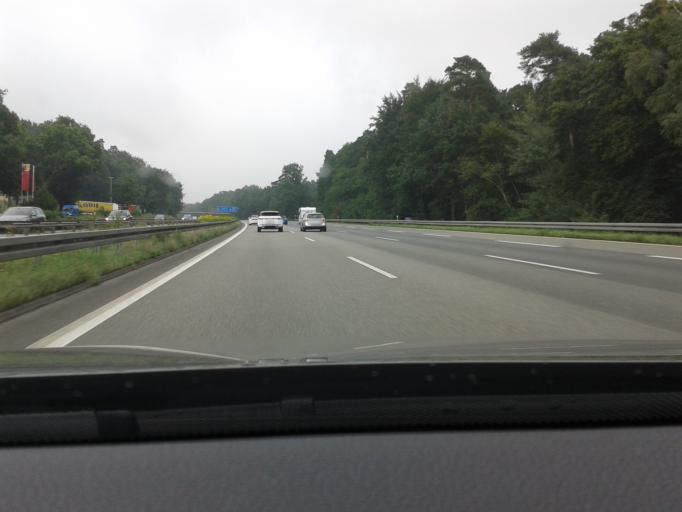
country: DE
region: North Rhine-Westphalia
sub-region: Regierungsbezirk Detmold
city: Verl
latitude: 51.9264
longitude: 8.5291
